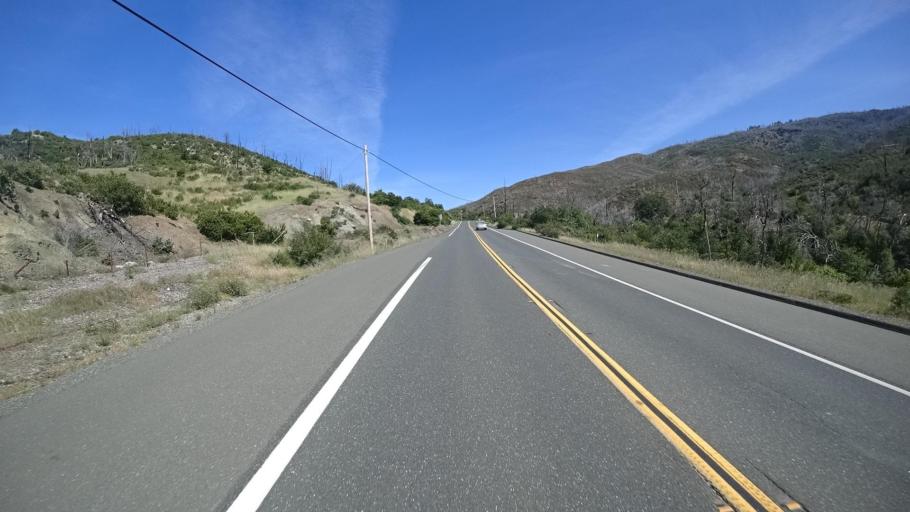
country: US
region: California
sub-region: Lake County
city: Cobb
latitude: 38.7891
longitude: -122.6944
